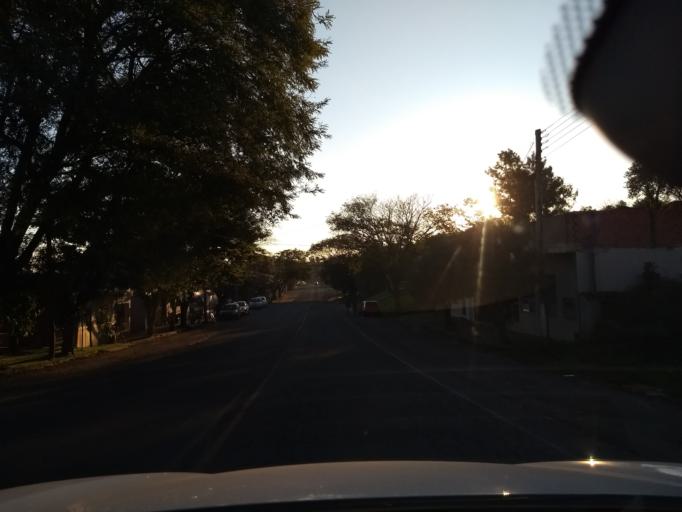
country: BR
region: Rio Grande do Sul
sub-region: Santa Cruz Do Sul
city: Santa Cruz do Sul
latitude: -29.7153
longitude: -52.5144
